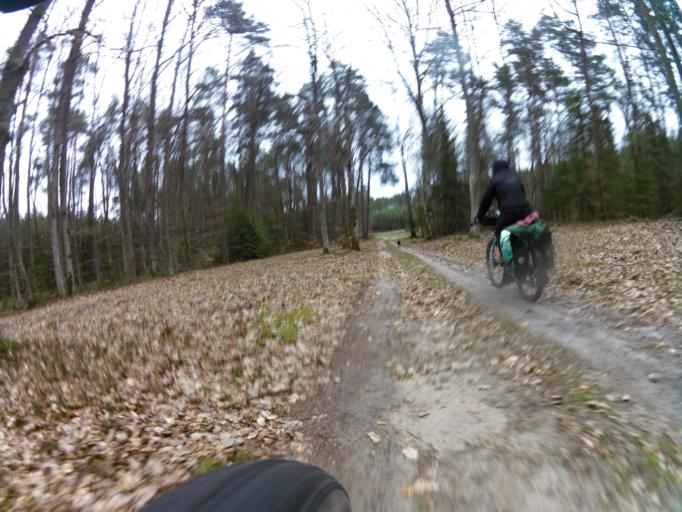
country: PL
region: West Pomeranian Voivodeship
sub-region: Powiat koszalinski
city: Polanow
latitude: 54.1674
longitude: 16.6447
